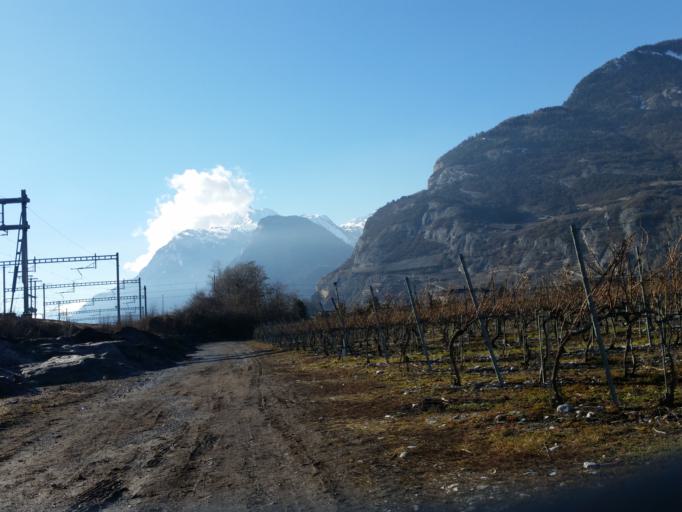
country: CH
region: Valais
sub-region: Conthey District
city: Ardon
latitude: 46.2098
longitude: 7.2751
